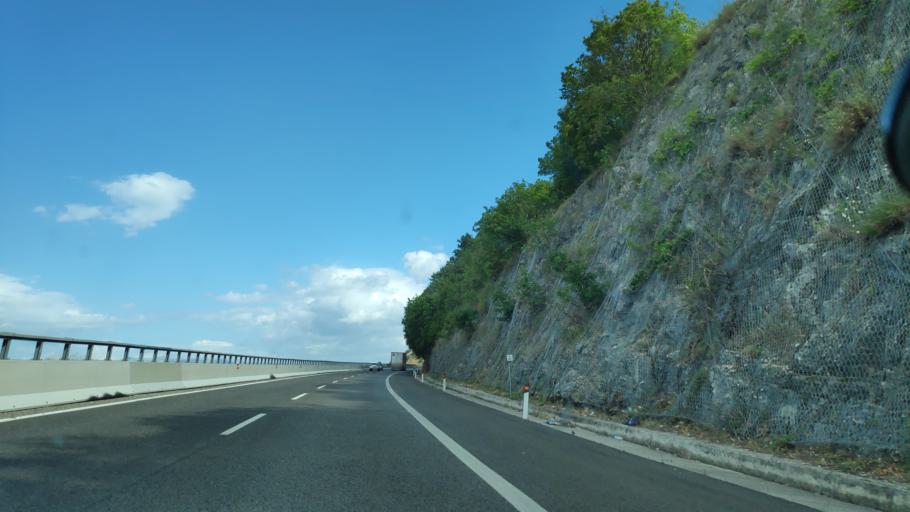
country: IT
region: Campania
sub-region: Provincia di Salerno
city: Sicignano degli Alburni
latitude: 40.5900
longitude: 15.3317
